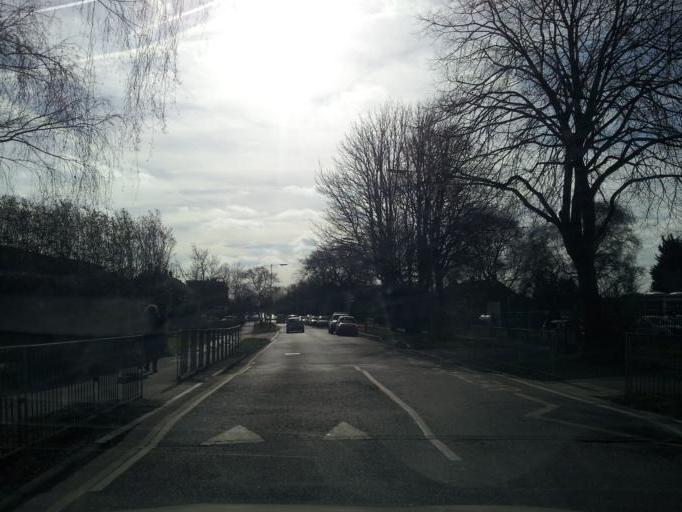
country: GB
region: England
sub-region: Hertfordshire
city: St Albans
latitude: 51.7452
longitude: -0.3142
